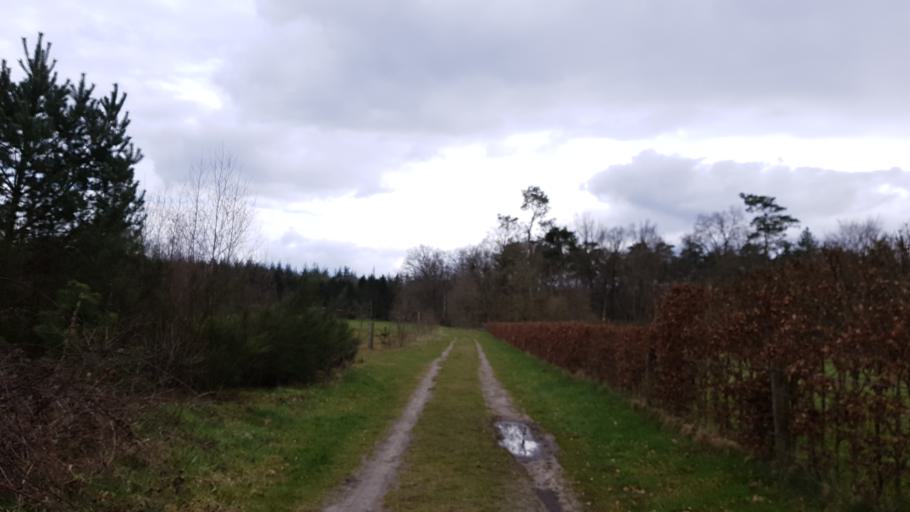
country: NL
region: Gelderland
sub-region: Gemeente Epe
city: Emst
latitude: 52.3155
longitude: 5.9146
